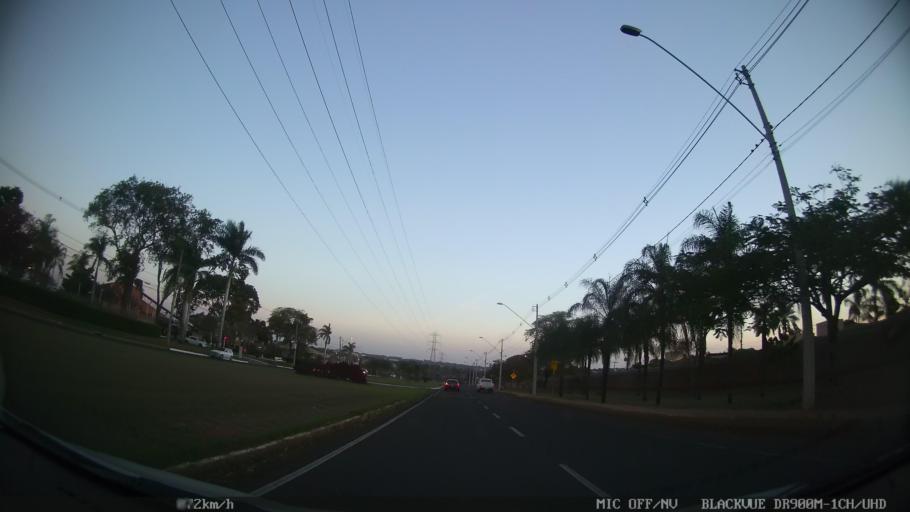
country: BR
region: Sao Paulo
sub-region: Sao Jose Do Rio Preto
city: Sao Jose do Rio Preto
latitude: -20.8216
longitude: -49.3406
